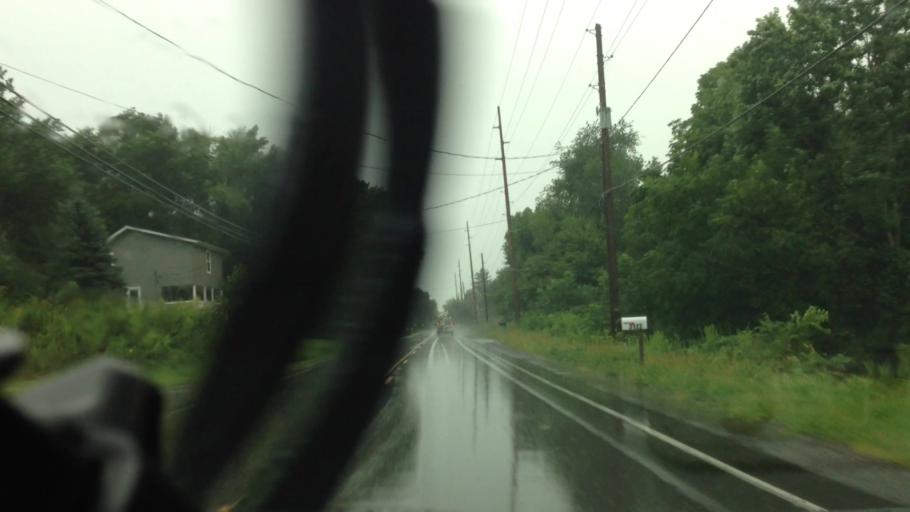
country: US
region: Ohio
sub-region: Stark County
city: Massillon
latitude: 40.8267
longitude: -81.5248
